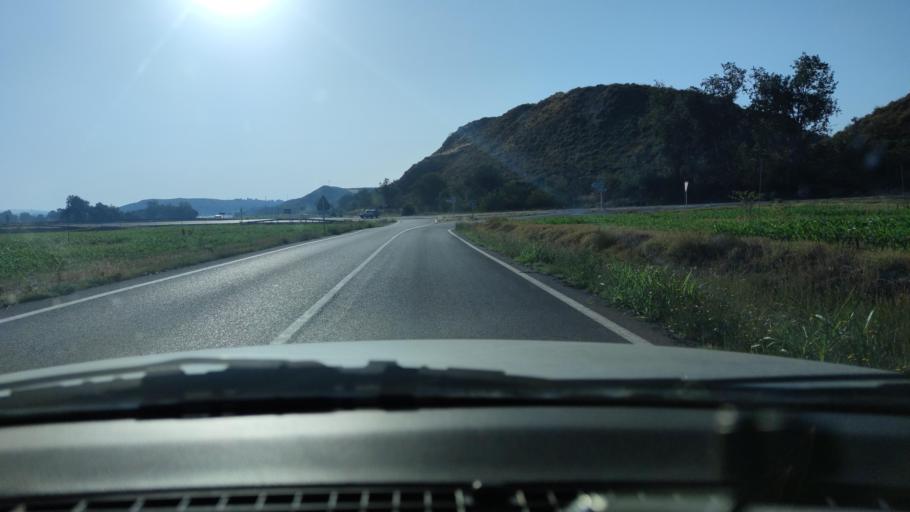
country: ES
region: Catalonia
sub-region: Provincia de Lleida
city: Balaguer
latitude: 41.8021
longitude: 0.8435
